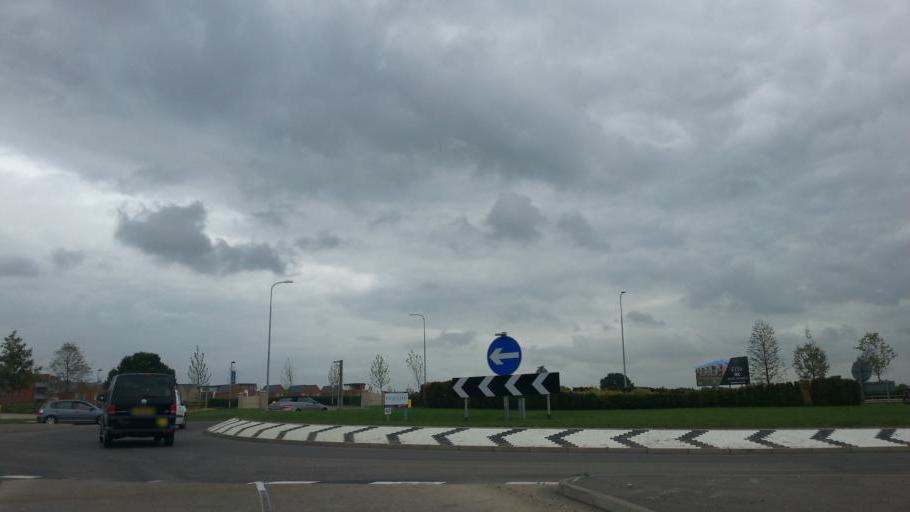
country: GB
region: England
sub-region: Essex
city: Chelmsford
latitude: 51.7652
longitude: 0.4888
